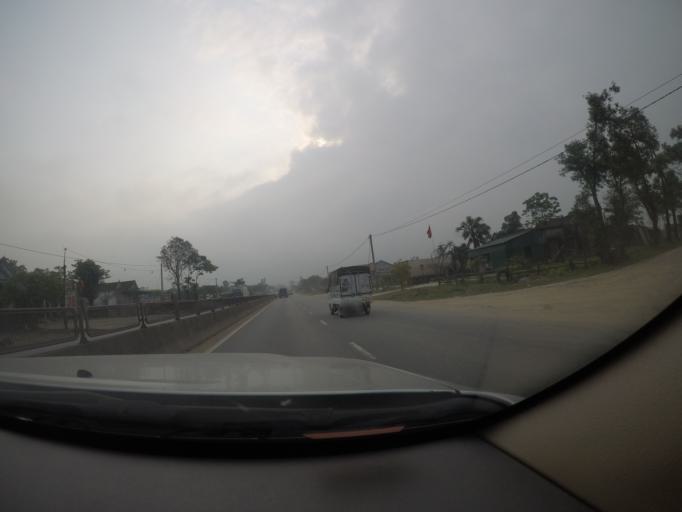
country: VN
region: Ha Tinh
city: Cam Xuyen
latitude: 18.2038
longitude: 106.1366
